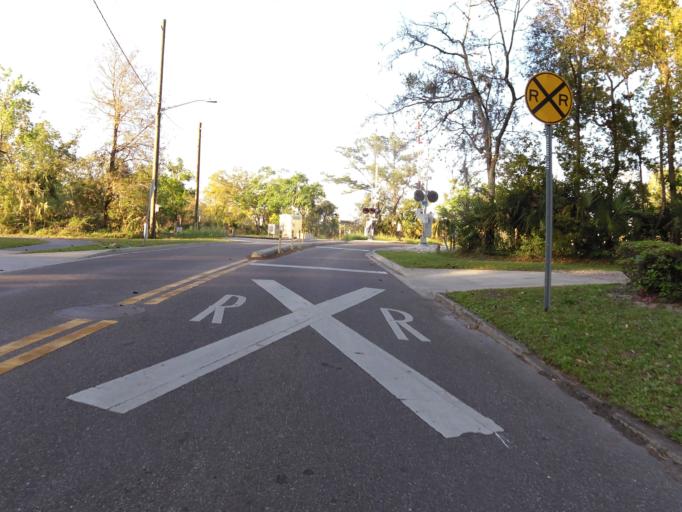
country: US
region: Florida
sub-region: Duval County
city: Jacksonville
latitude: 30.2998
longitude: -81.6454
